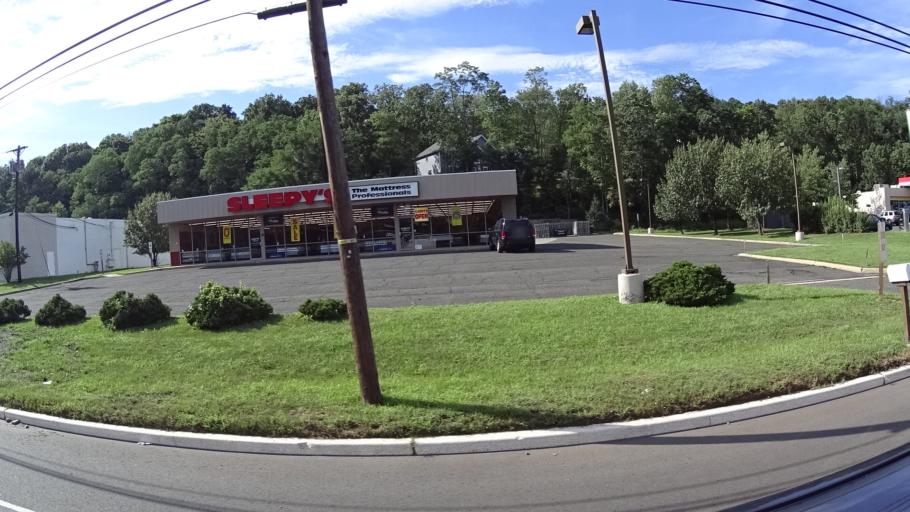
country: US
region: New Jersey
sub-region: Middlesex County
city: Dunellen
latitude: 40.5953
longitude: -74.4912
